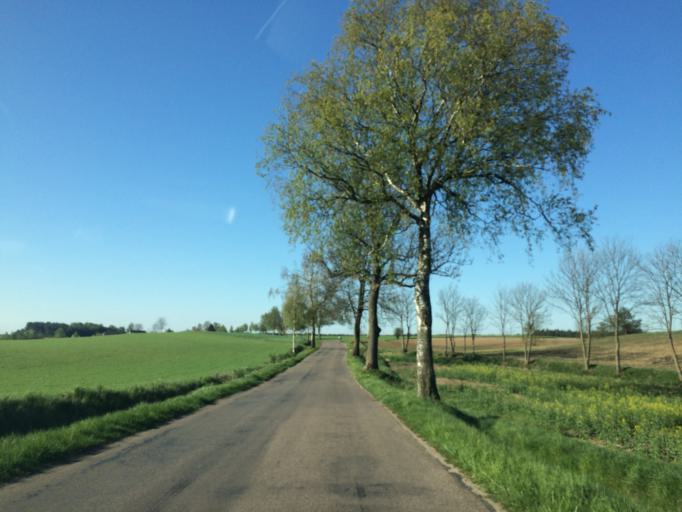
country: PL
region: Warmian-Masurian Voivodeship
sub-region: Powiat dzialdowski
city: Rybno
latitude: 53.4090
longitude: 19.9366
